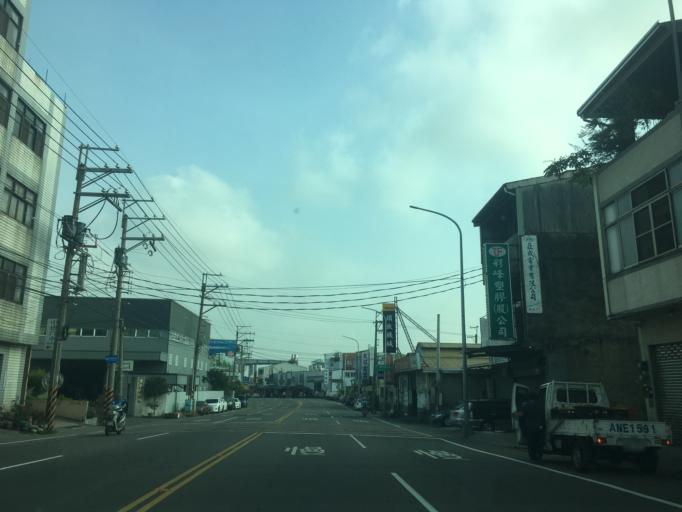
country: TW
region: Taiwan
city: Fengyuan
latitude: 24.2284
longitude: 120.7245
